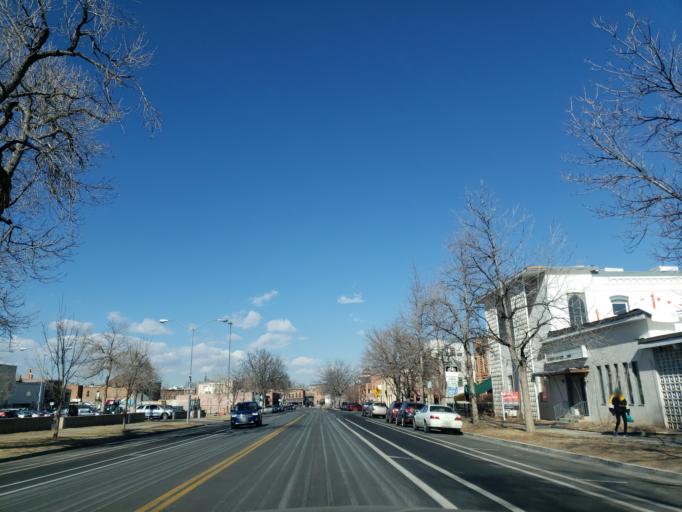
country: US
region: Colorado
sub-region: Larimer County
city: Fort Collins
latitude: 40.5848
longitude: -105.0755
